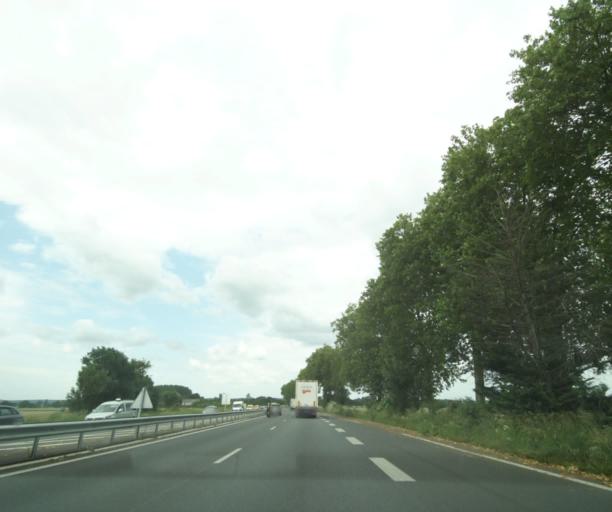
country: FR
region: Pays de la Loire
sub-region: Departement de Maine-et-Loire
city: Villebernier
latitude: 47.2871
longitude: -0.0472
